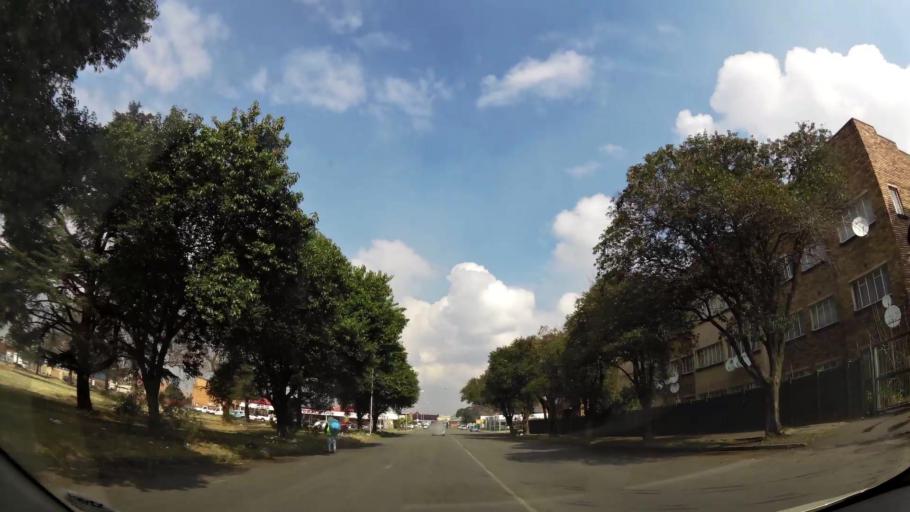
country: ZA
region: Gauteng
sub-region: Sedibeng District Municipality
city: Vereeniging
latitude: -26.6815
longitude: 27.9279
